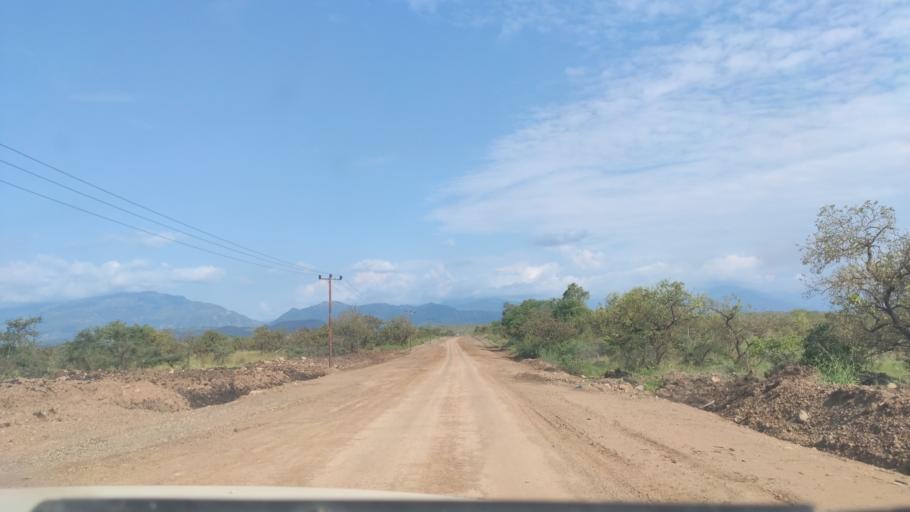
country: ET
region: Southern Nations, Nationalities, and People's Region
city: Felege Neway
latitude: 6.4266
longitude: 37.2279
